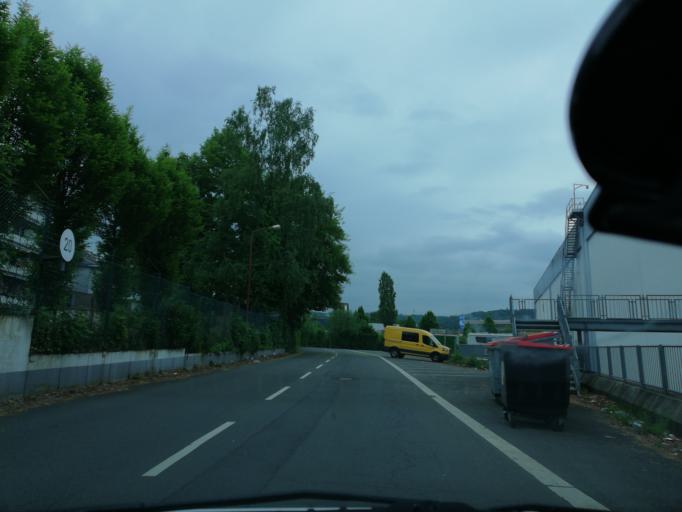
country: DE
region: North Rhine-Westphalia
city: Wetter (Ruhr)
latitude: 51.3830
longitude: 7.3896
